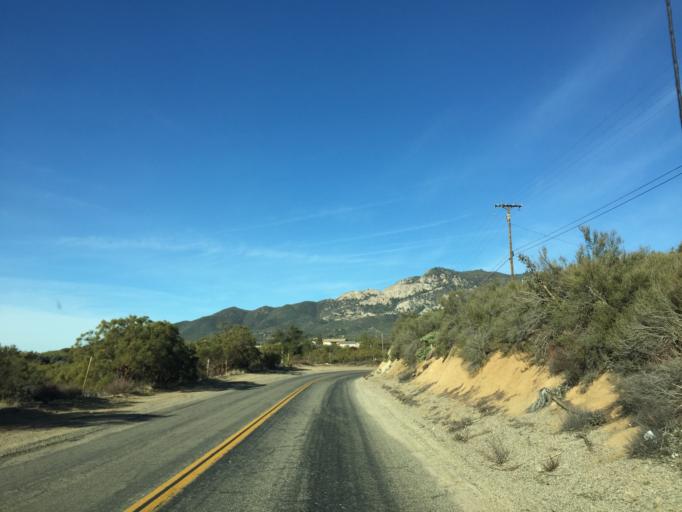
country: US
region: California
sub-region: Riverside County
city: Anza
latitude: 33.5696
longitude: -116.7413
